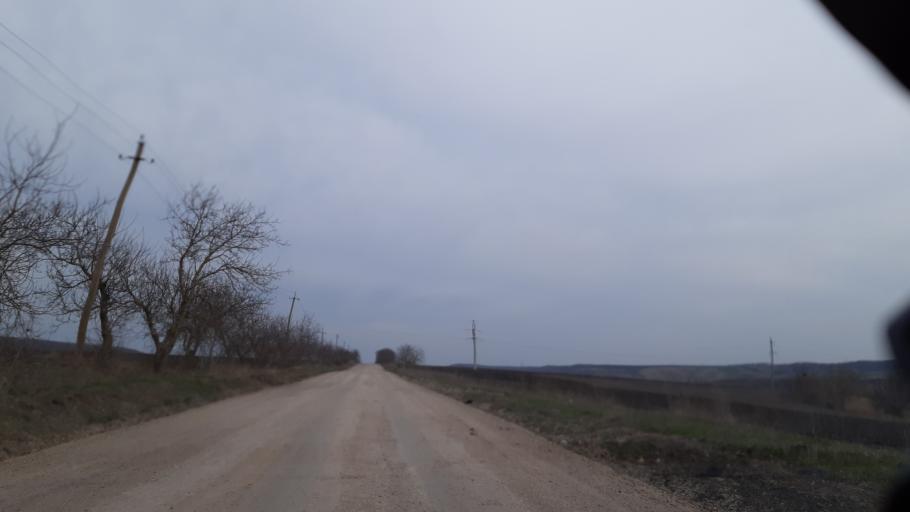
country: MD
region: Soldanesti
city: Soldanesti
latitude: 47.7031
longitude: 28.7183
